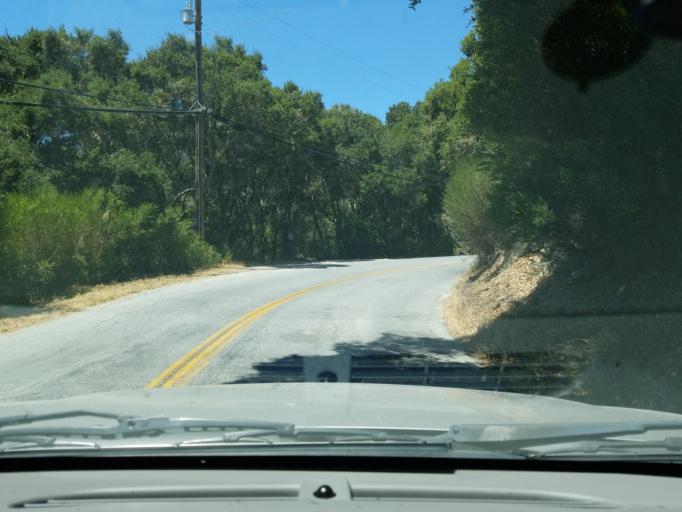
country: US
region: California
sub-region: Monterey County
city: Carmel Valley Village
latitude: 36.4592
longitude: -121.7072
